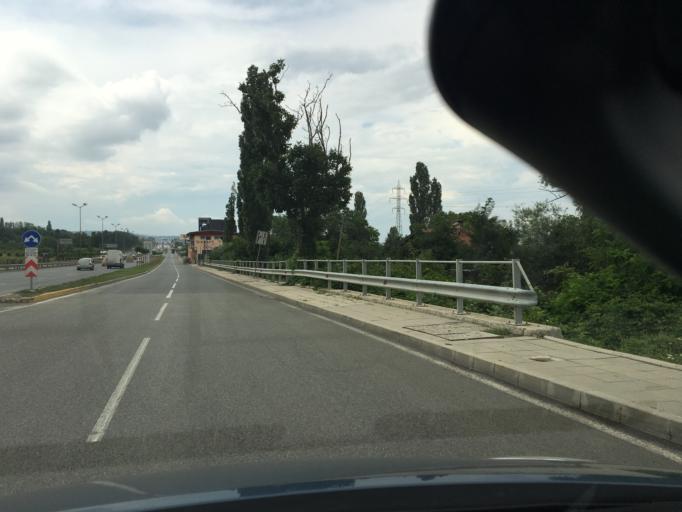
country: BG
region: Sofia-Capital
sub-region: Stolichna Obshtina
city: Sofia
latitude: 42.6438
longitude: 23.3075
